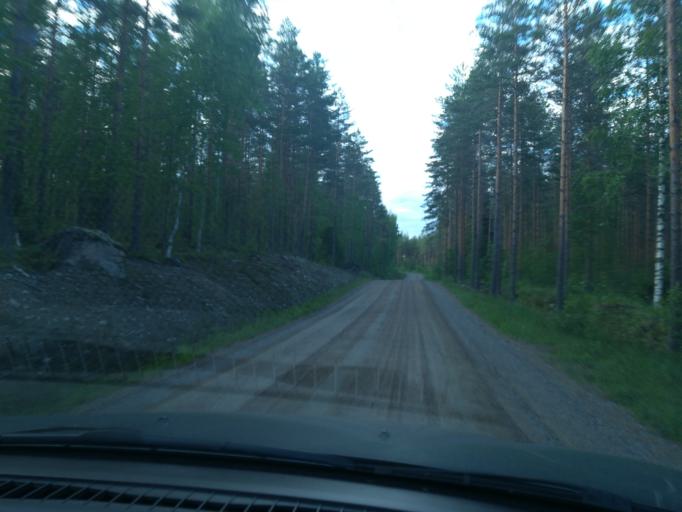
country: FI
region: Southern Savonia
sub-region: Mikkeli
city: Puumala
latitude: 61.5812
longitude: 28.1649
